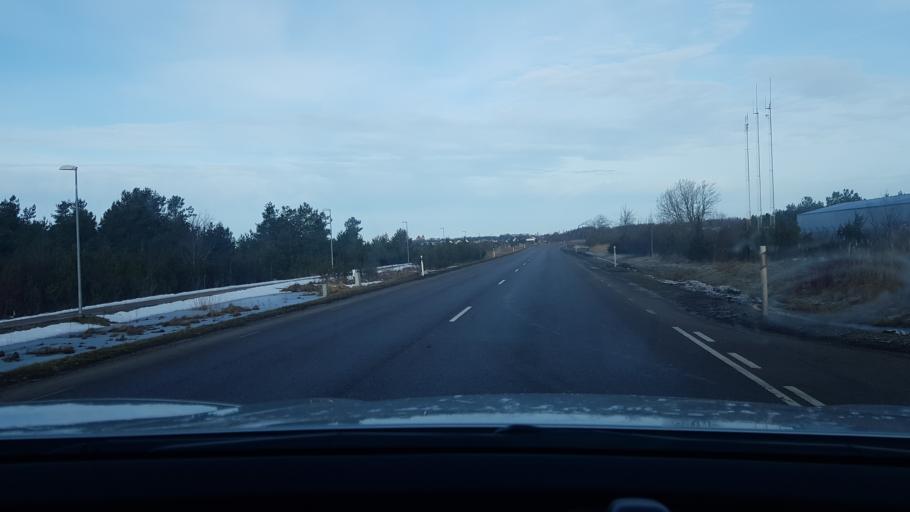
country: EE
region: Saare
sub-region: Kuressaare linn
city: Kuressaare
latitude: 58.2322
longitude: 22.5035
